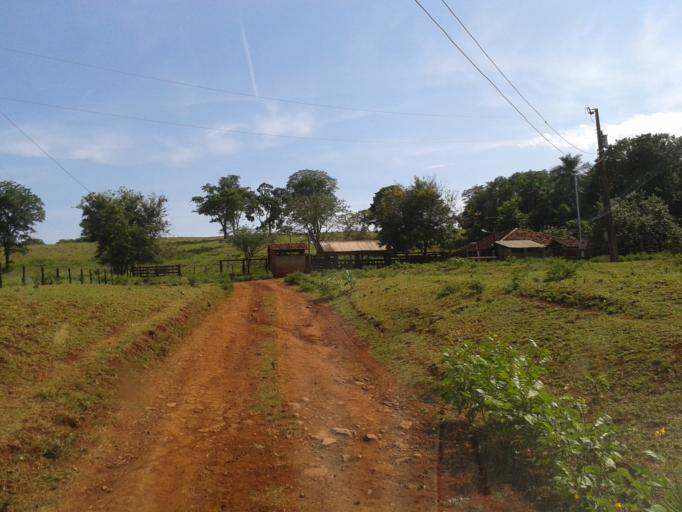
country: BR
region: Minas Gerais
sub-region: Centralina
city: Centralina
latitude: -18.6931
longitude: -49.2097
